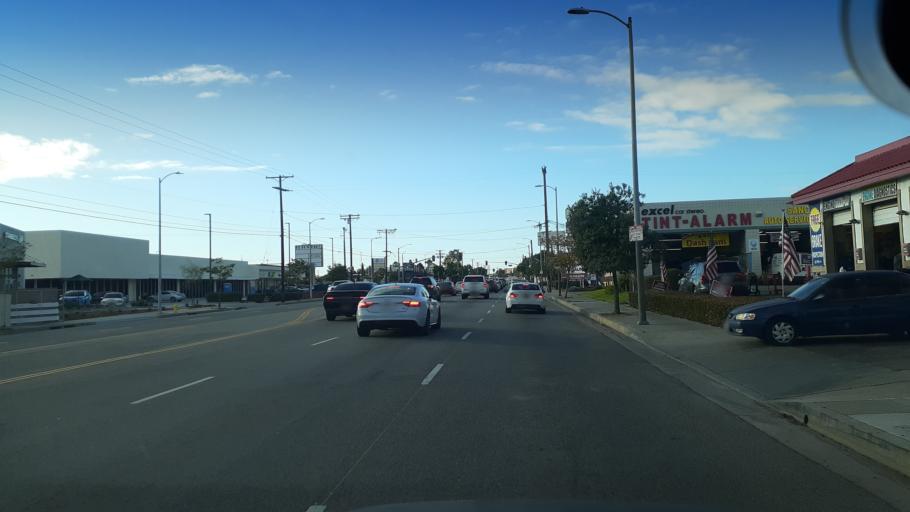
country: US
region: California
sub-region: Los Angeles County
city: West Carson
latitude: 33.8164
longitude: -118.3070
